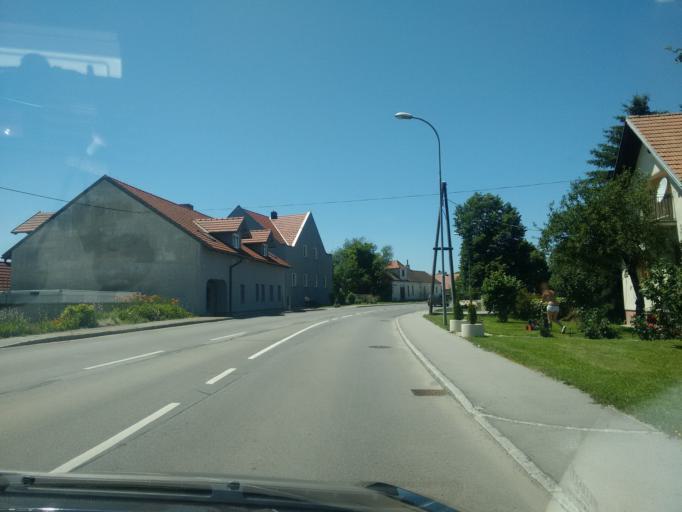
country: AT
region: Lower Austria
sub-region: Politischer Bezirk Sankt Polten
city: Kapelln
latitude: 48.2599
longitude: 15.8012
